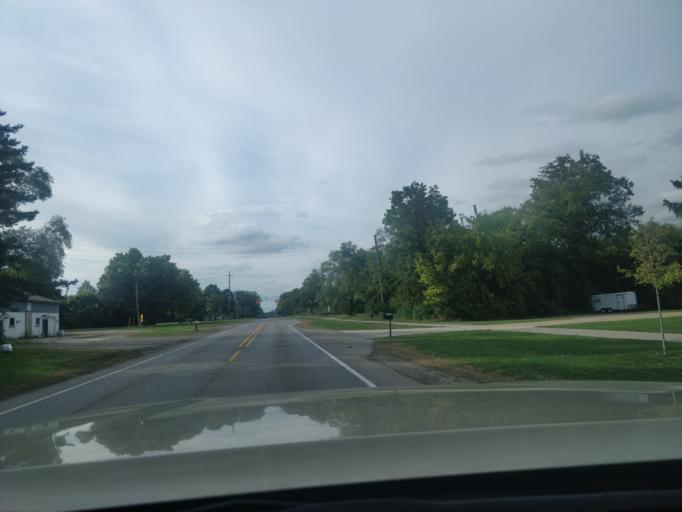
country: US
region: Michigan
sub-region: Wayne County
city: Romulus
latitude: 42.2105
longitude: -83.4031
